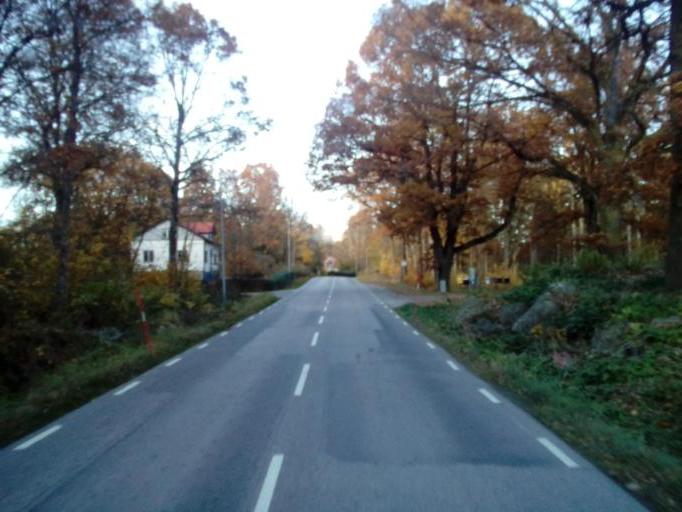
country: SE
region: Kalmar
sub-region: Vimmerby Kommun
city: Vimmerby
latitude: 57.7240
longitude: 16.0692
